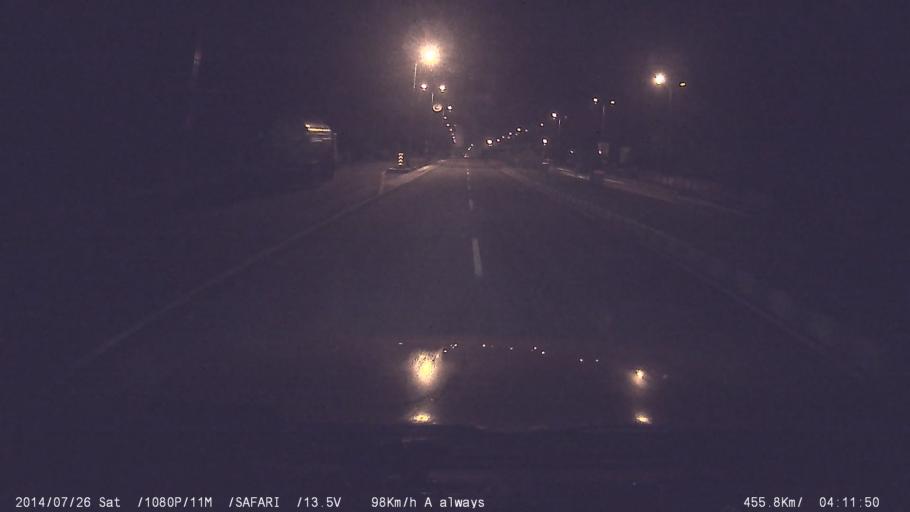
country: IN
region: Kerala
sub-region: Thrissur District
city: Trichur
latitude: 10.5007
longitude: 76.2582
